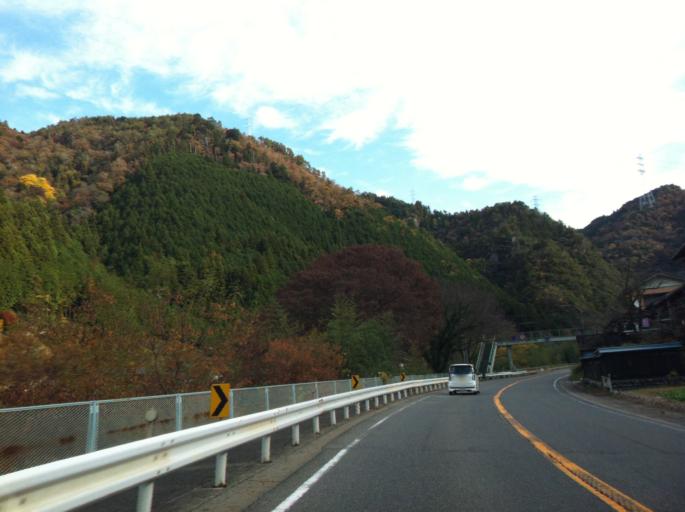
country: JP
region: Gifu
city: Mitake
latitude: 35.5521
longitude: 137.1651
